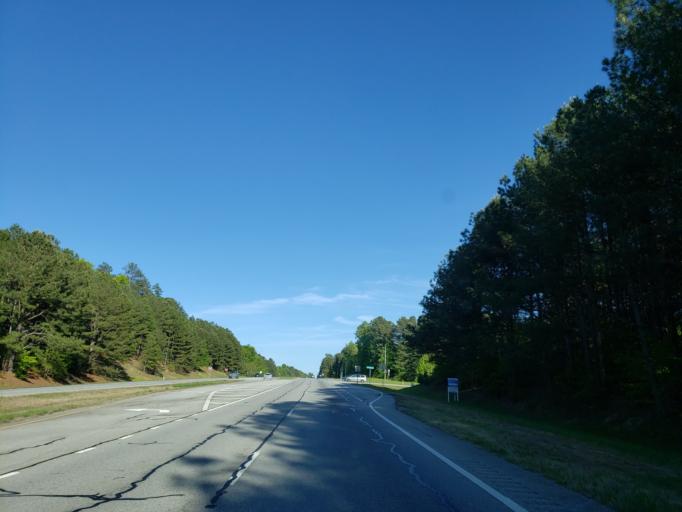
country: US
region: Georgia
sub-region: Polk County
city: Rockmart
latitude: 33.9291
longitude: -84.9549
